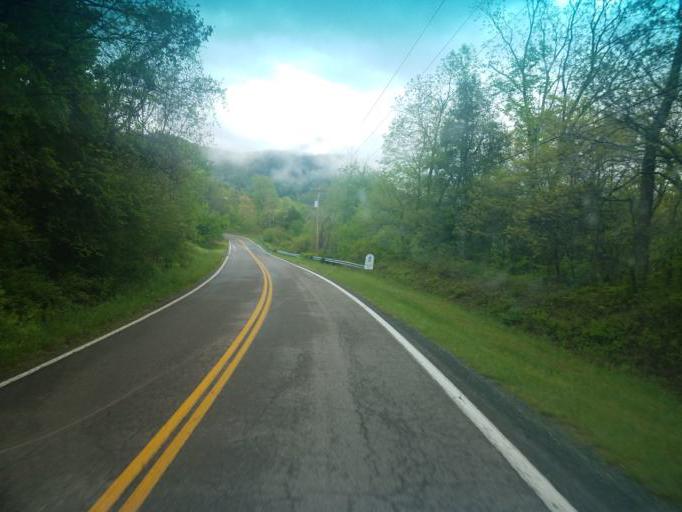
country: US
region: Virginia
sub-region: Washington County
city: Emory
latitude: 36.6374
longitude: -81.7907
